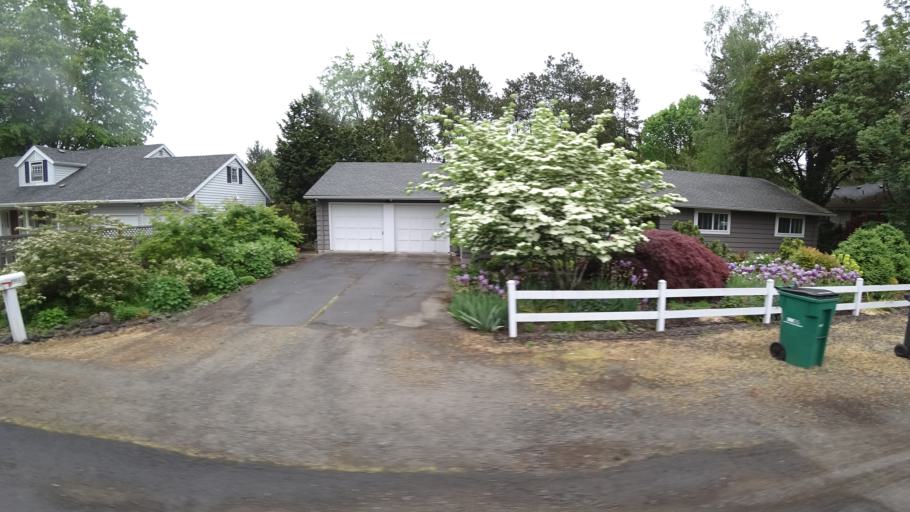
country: US
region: Oregon
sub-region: Washington County
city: Raleigh Hills
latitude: 45.4809
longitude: -122.7693
